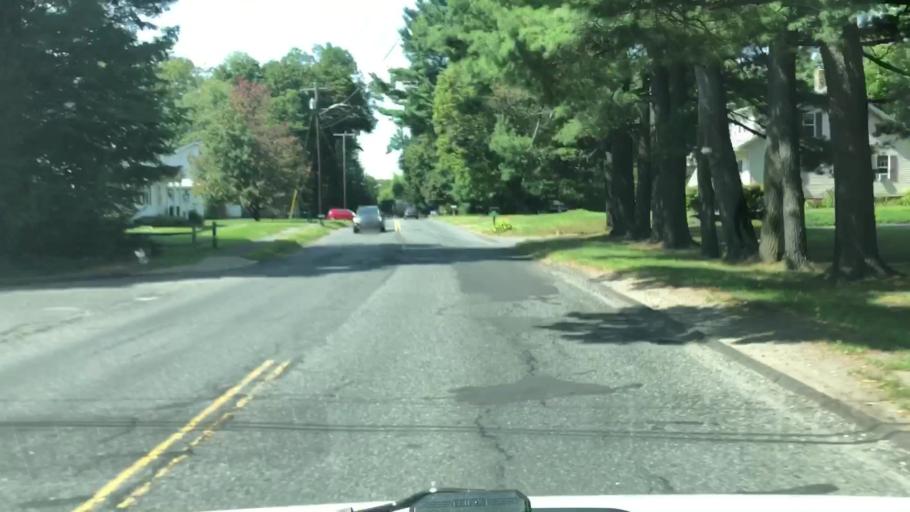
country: US
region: Massachusetts
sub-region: Hampshire County
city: Northampton
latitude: 42.3408
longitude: -72.6599
